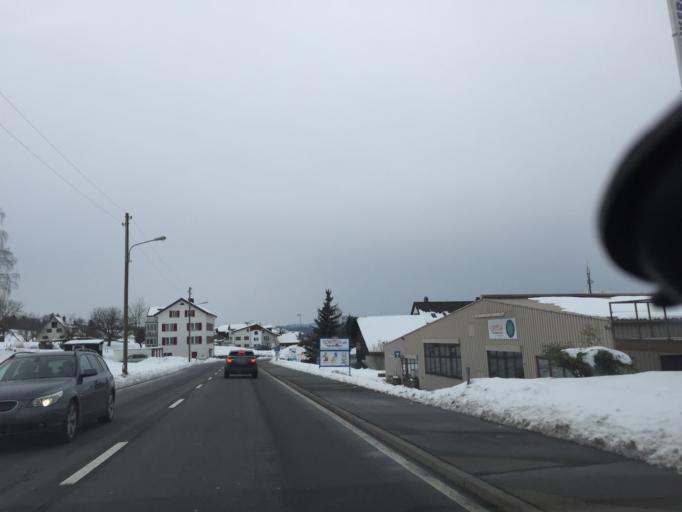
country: CH
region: Zurich
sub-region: Bezirk Horgen
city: Richterswil / Burghalde
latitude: 47.1881
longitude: 8.6798
